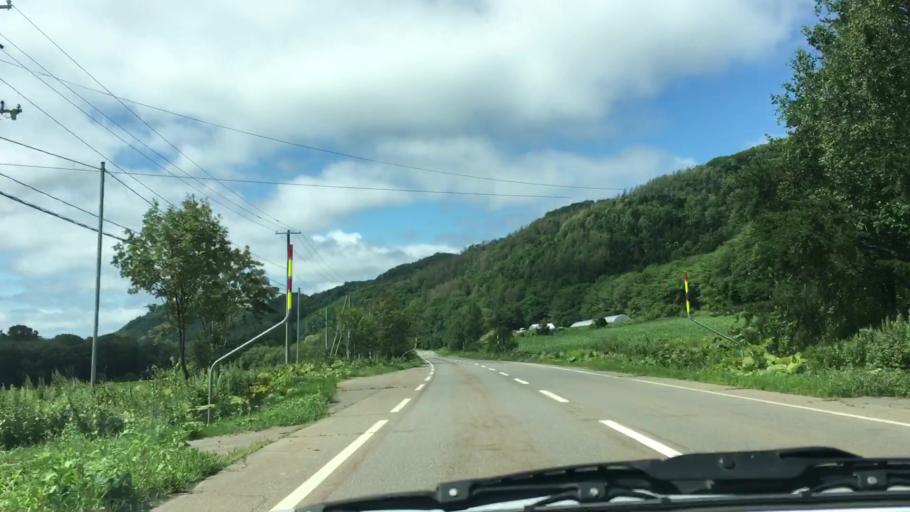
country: JP
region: Hokkaido
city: Kitami
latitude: 43.3611
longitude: 143.8331
